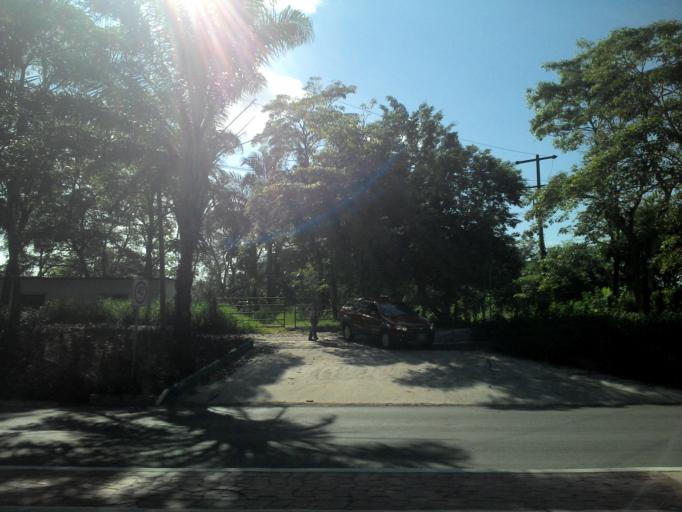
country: MX
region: Chiapas
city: Palenque
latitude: 17.5268
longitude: -91.9922
